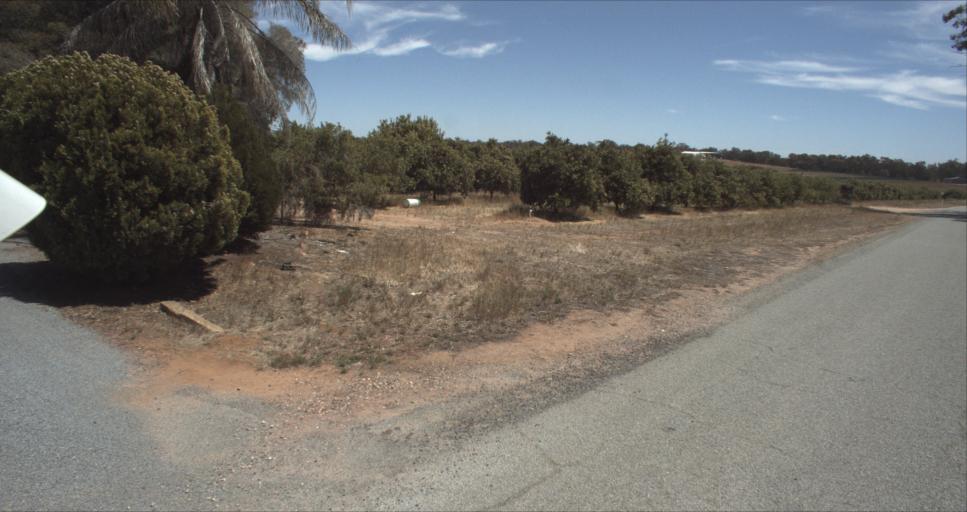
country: AU
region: New South Wales
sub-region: Leeton
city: Leeton
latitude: -34.6762
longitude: 146.4342
